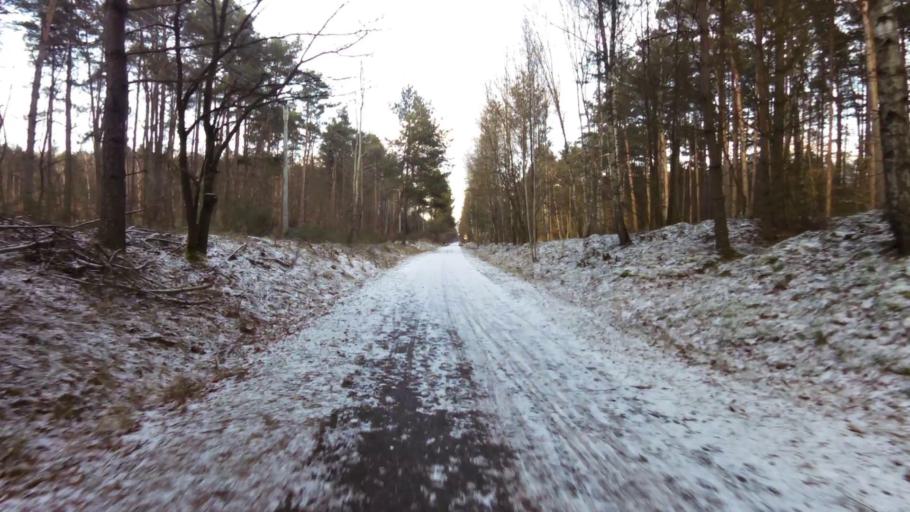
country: PL
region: West Pomeranian Voivodeship
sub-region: Powiat drawski
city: Zlocieniec
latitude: 53.5525
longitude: 16.0215
